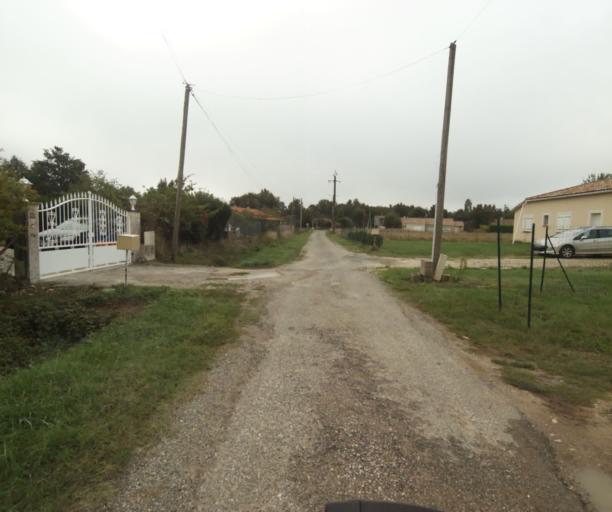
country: FR
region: Midi-Pyrenees
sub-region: Departement du Tarn-et-Garonne
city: Labastide-Saint-Pierre
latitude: 43.8862
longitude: 1.3787
